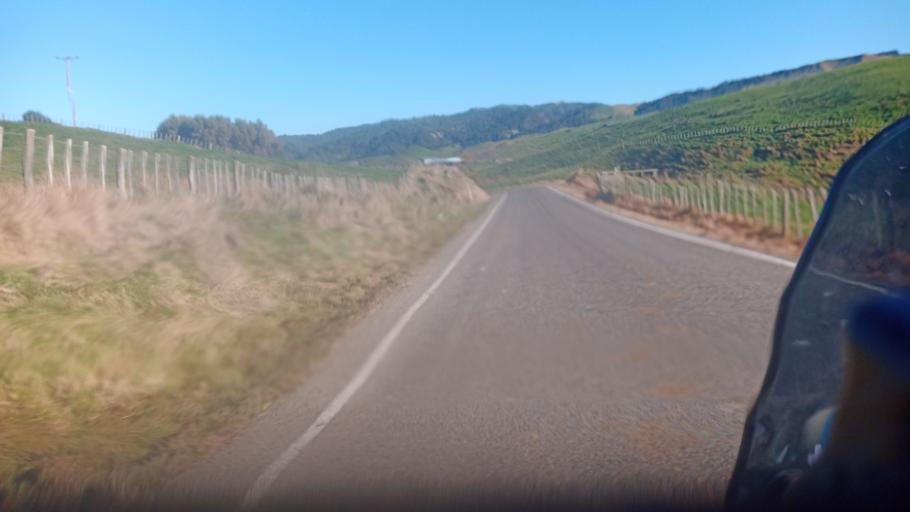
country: NZ
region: Gisborne
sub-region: Gisborne District
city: Gisborne
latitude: -38.5791
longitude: 177.5579
